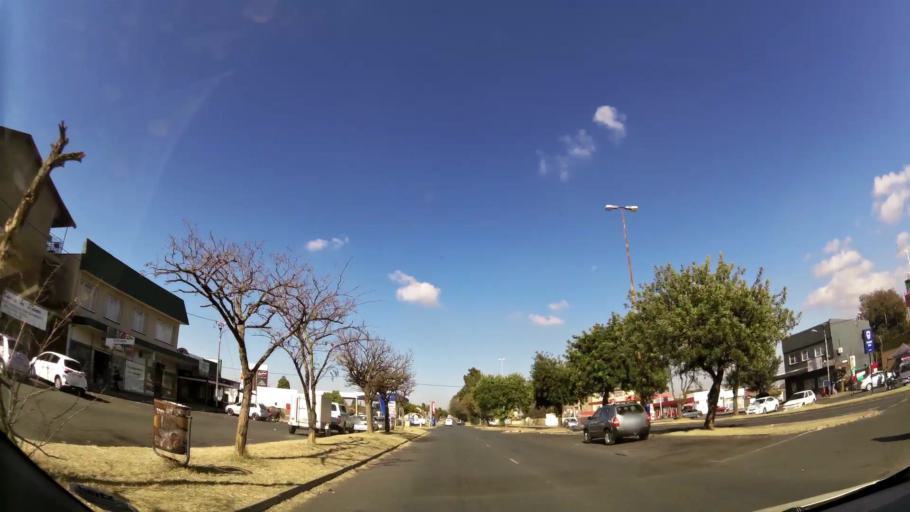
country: ZA
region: Gauteng
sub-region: City of Johannesburg Metropolitan Municipality
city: Roodepoort
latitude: -26.1336
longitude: 27.8350
